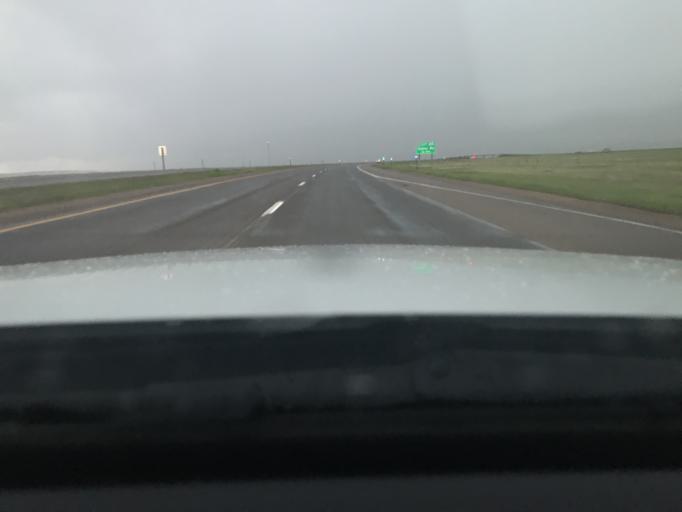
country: US
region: Wyoming
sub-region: Platte County
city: Wheatland
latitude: 41.8823
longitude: -104.8821
